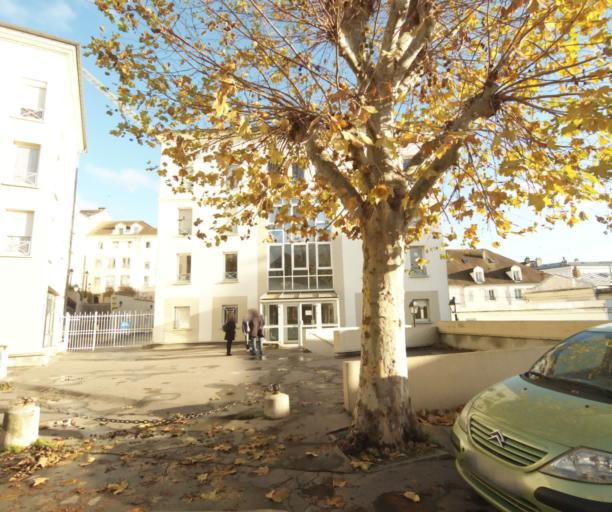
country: FR
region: Ile-de-France
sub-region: Departement des Yvelines
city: Meulan-en-Yvelines
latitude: 49.0054
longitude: 1.9099
